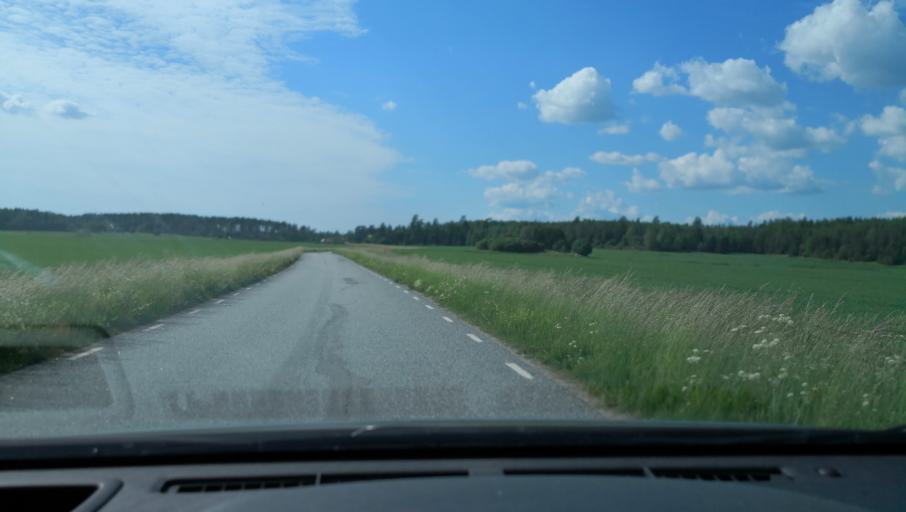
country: SE
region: Uppsala
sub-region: Enkopings Kommun
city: Orsundsbro
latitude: 59.8369
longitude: 17.3016
